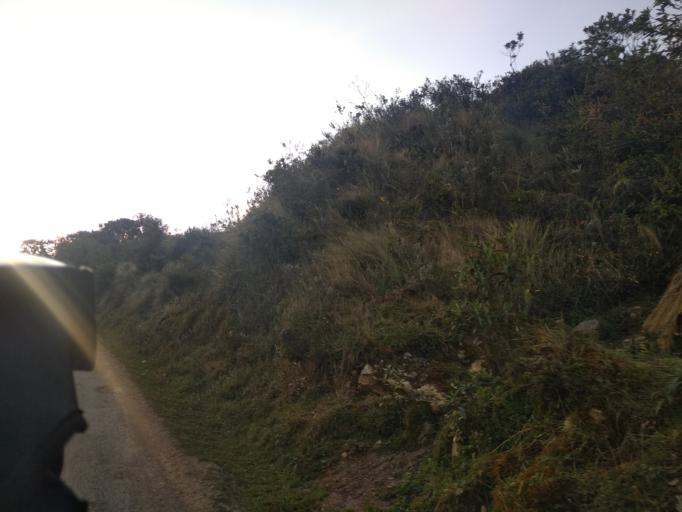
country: PE
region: Amazonas
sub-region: Provincia de Chachapoyas
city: Montevideo
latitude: -6.7098
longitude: -77.8684
